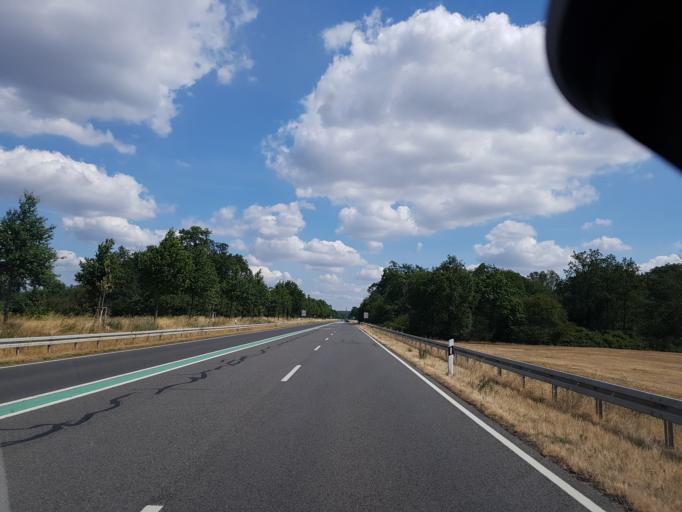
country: DE
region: Brandenburg
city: Drebkau
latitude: 51.6753
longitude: 14.2511
